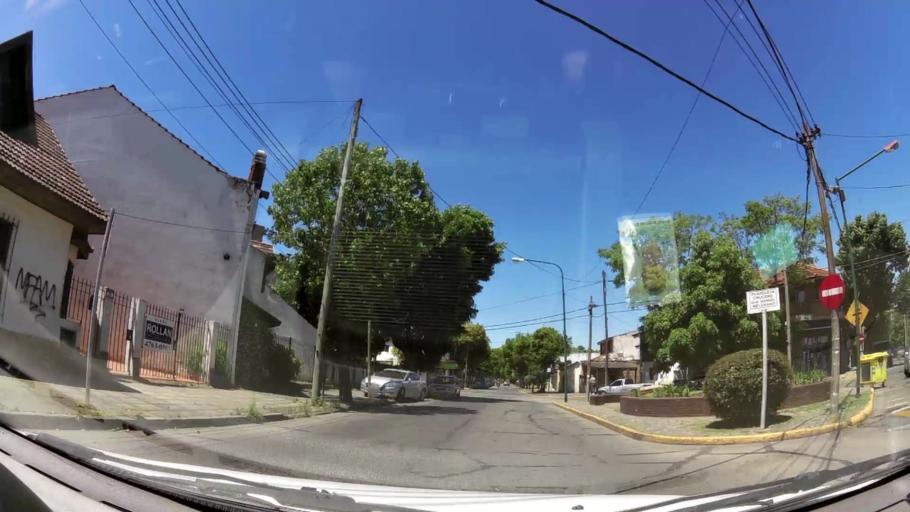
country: AR
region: Buenos Aires
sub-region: Partido de San Isidro
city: San Isidro
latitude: -34.4916
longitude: -58.5128
